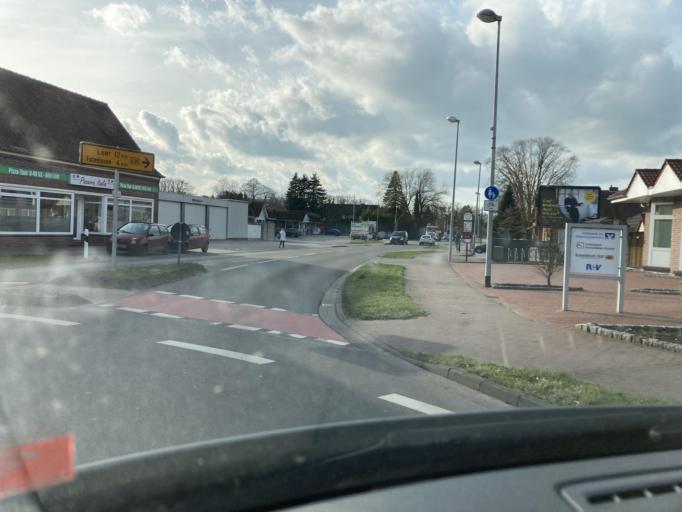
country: DE
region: Lower Saxony
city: Nortmoor
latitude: 53.1594
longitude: 7.5298
